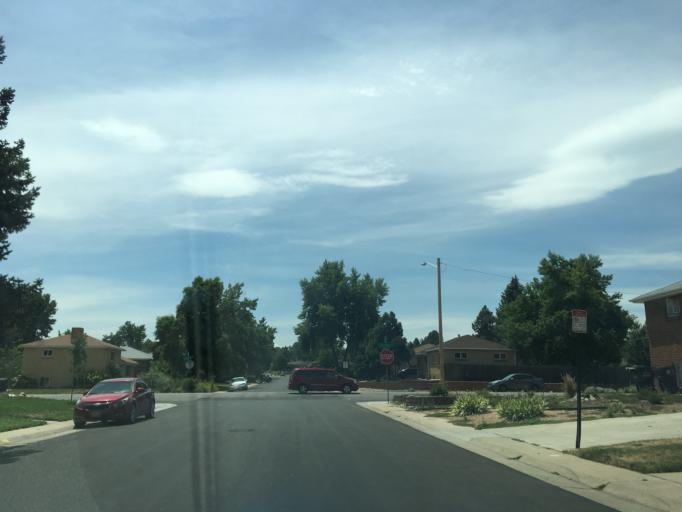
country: US
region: Colorado
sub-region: Jefferson County
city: Lakewood
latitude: 39.6797
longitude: -105.0511
